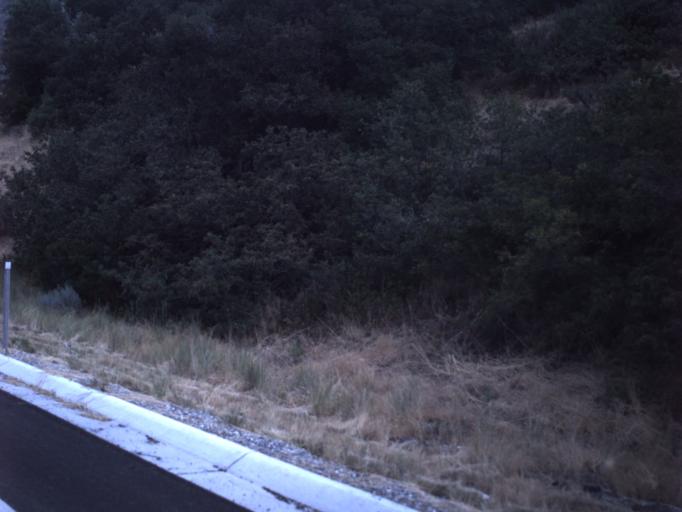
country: US
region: Utah
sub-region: Salt Lake County
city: Cottonwood Heights
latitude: 40.6054
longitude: -111.7942
